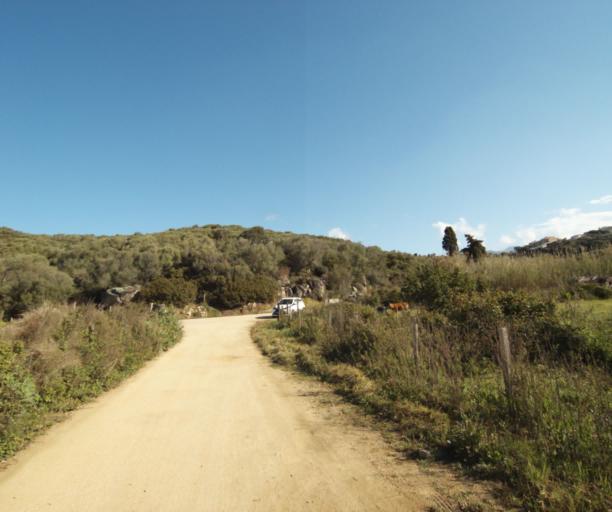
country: FR
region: Corsica
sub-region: Departement de la Corse-du-Sud
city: Propriano
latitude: 41.6647
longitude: 8.8927
